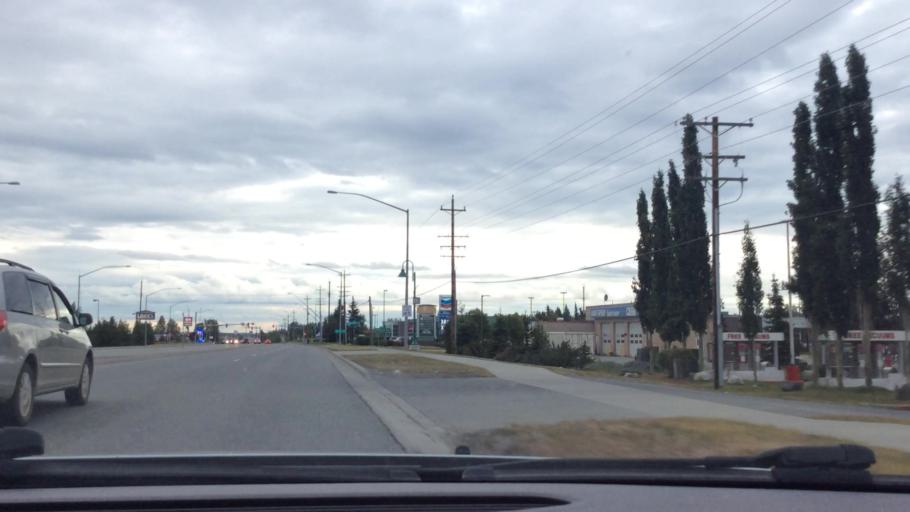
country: US
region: Alaska
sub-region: Anchorage Municipality
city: Anchorage
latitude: 61.1201
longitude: -149.8631
